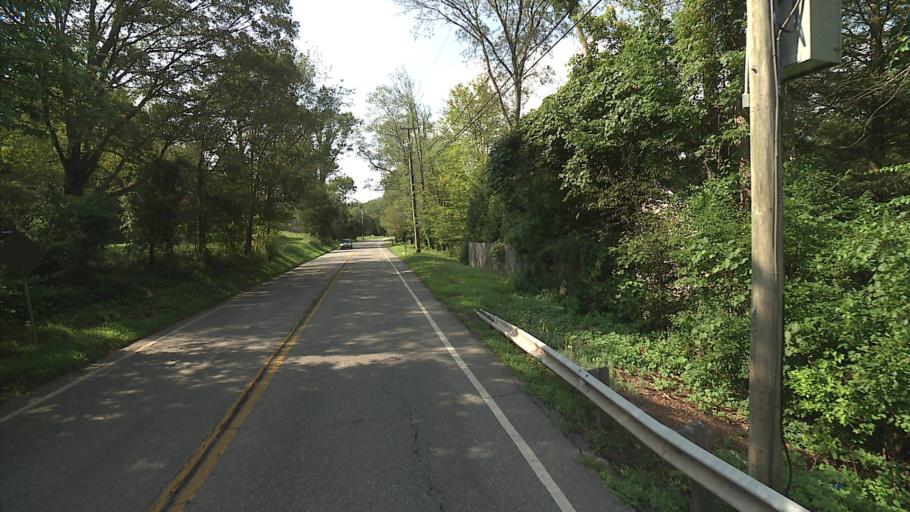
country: US
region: Connecticut
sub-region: Middlesex County
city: Moodus
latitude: 41.4883
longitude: -72.4659
